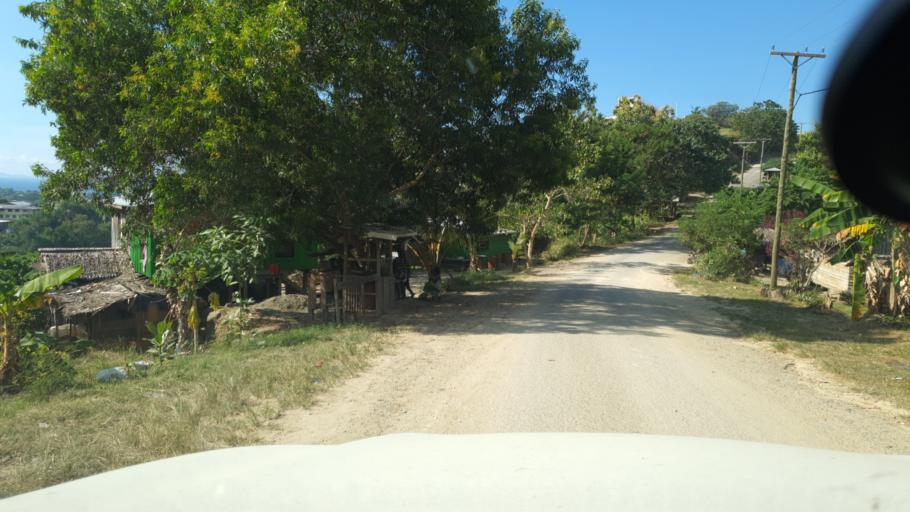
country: SB
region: Guadalcanal
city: Honiara
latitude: -9.4564
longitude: 159.9785
